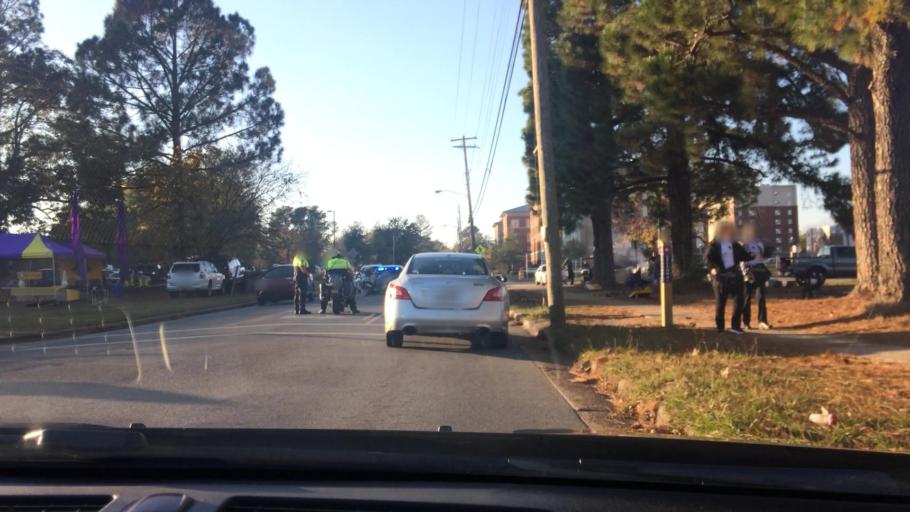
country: US
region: North Carolina
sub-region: Pitt County
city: Greenville
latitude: 35.5982
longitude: -77.3623
